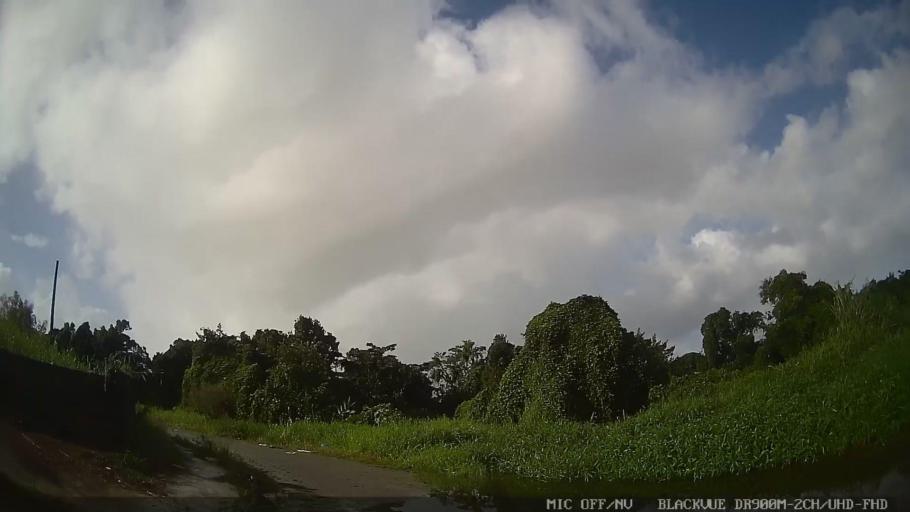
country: BR
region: Sao Paulo
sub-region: Itanhaem
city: Itanhaem
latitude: -24.1949
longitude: -46.8245
